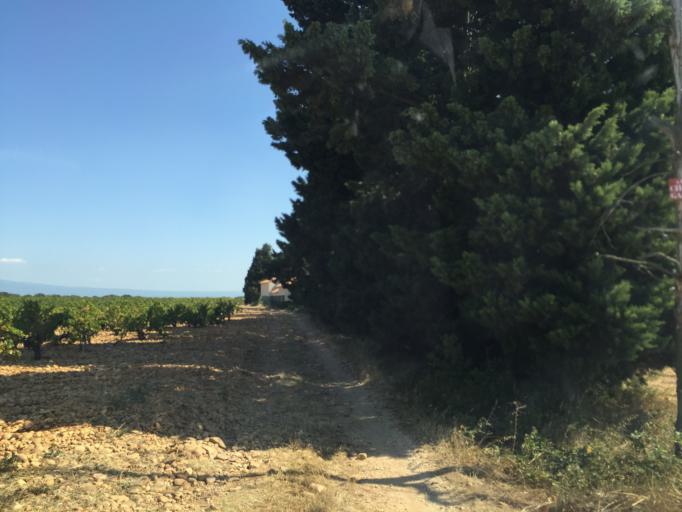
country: FR
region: Provence-Alpes-Cote d'Azur
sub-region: Departement du Vaucluse
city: Orange
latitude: 44.1065
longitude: 4.8365
